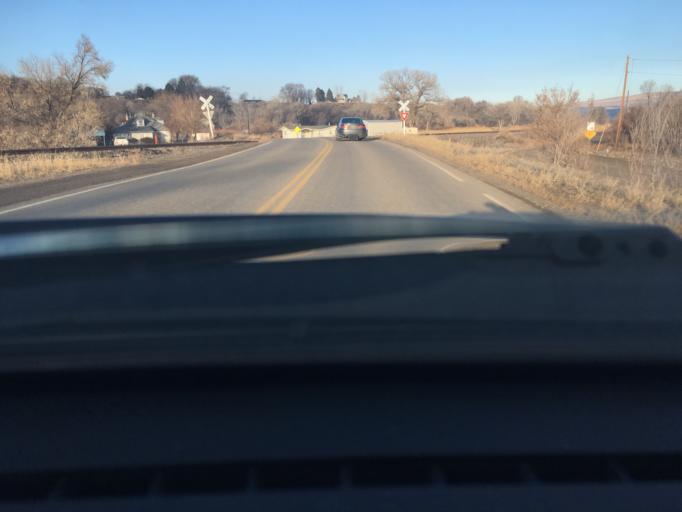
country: US
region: Colorado
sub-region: Delta County
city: Delta
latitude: 38.7407
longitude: -108.0817
